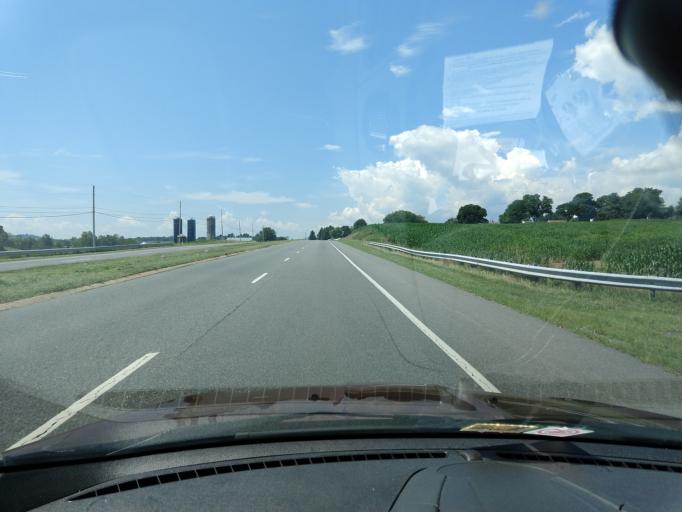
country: US
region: Virginia
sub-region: City of Harrisonburg
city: Harrisonburg
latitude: 38.5165
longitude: -78.8652
